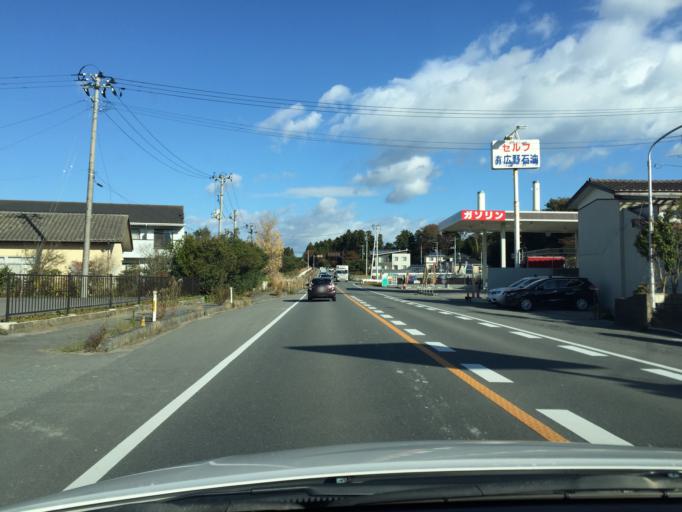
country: JP
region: Fukushima
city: Iwaki
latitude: 37.2207
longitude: 141.0020
